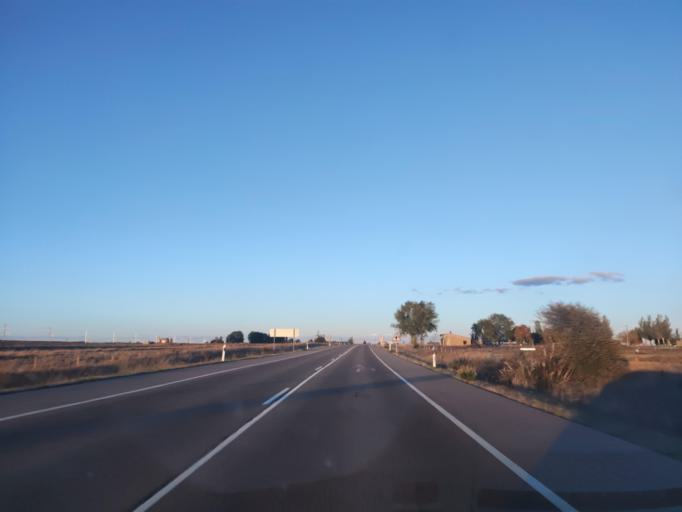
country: ES
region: Castille and Leon
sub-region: Provincia de Salamanca
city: La Fuente de San Esteban
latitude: 40.7844
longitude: -6.2615
